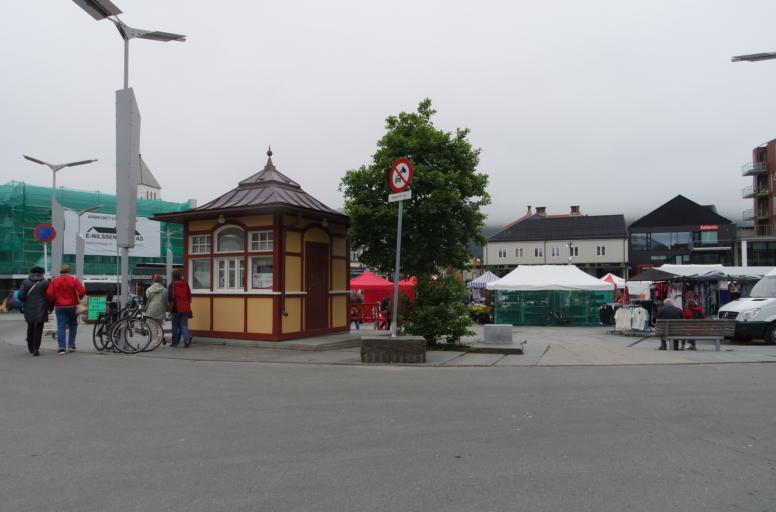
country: NO
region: Nordland
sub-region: Vagan
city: Svolvaer
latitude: 68.2317
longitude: 14.5642
